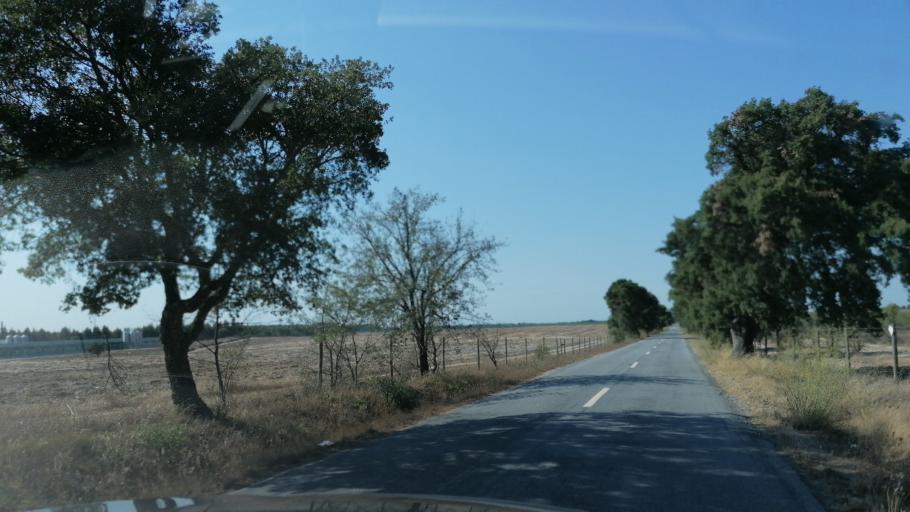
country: PT
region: Evora
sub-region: Vendas Novas
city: Vendas Novas
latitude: 38.7228
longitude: -8.6202
